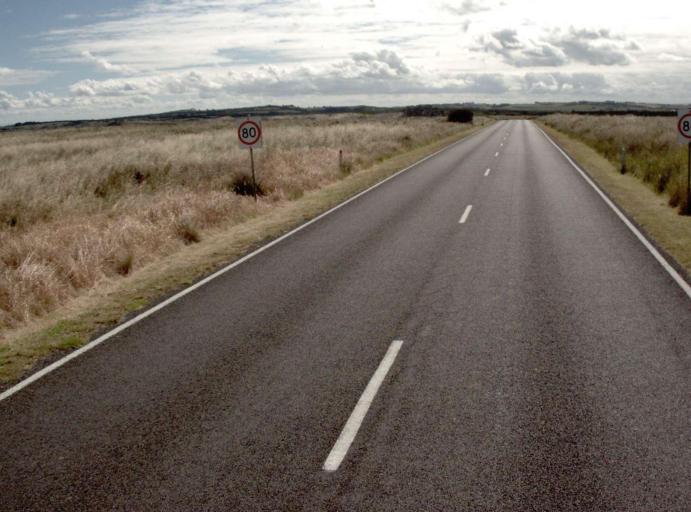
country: AU
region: Victoria
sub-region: Bass Coast
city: Phillip Island
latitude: -38.5108
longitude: 145.1267
